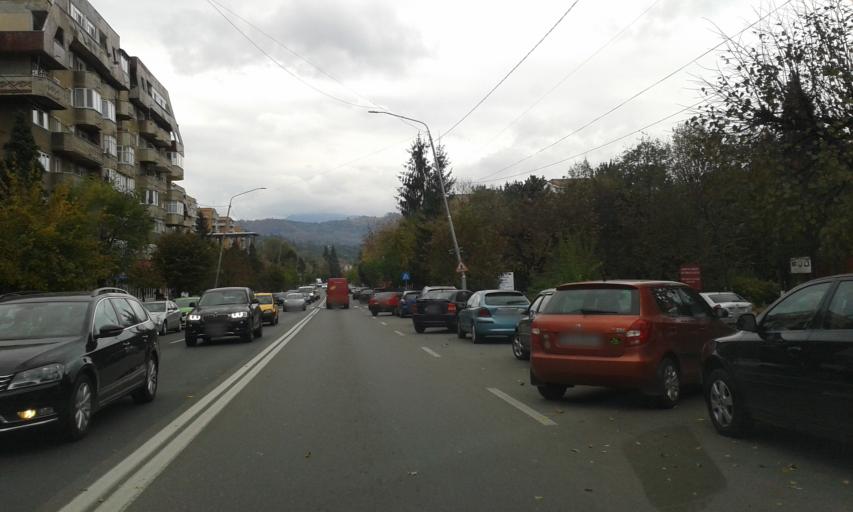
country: RO
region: Hunedoara
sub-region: Municipiul Petrosani
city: Petrosani
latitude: 45.4146
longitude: 23.3741
